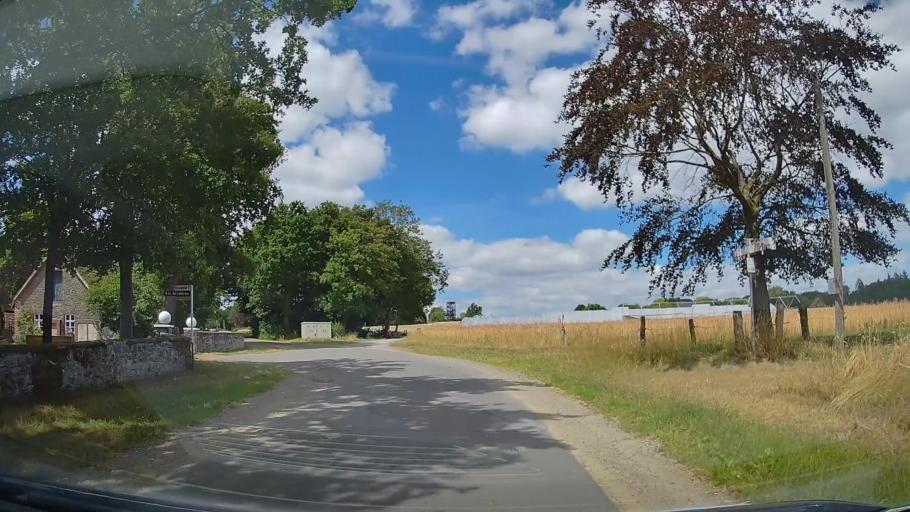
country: DE
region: Lower Saxony
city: Belm
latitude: 52.3868
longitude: 8.1339
